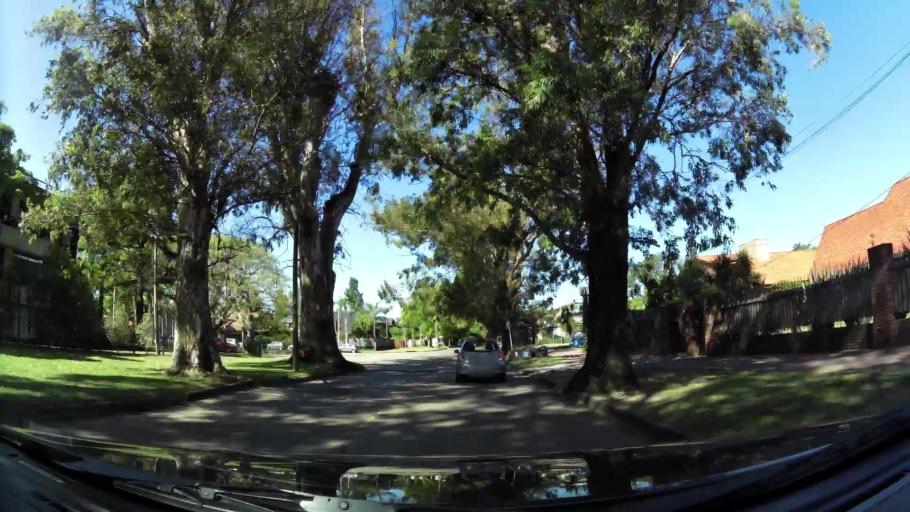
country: UY
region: Canelones
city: Paso de Carrasco
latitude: -34.8895
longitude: -56.0680
